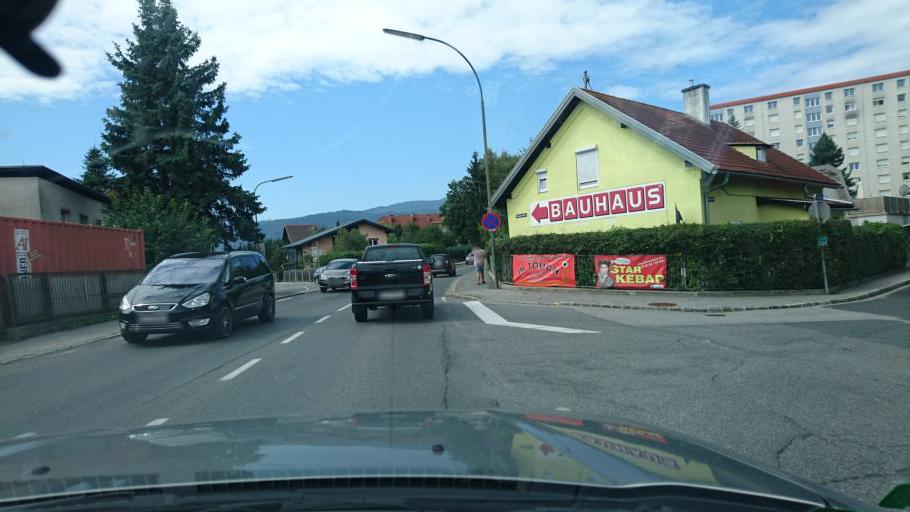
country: AT
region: Carinthia
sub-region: Villach Stadt
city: Villach
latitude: 46.6069
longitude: 13.8572
